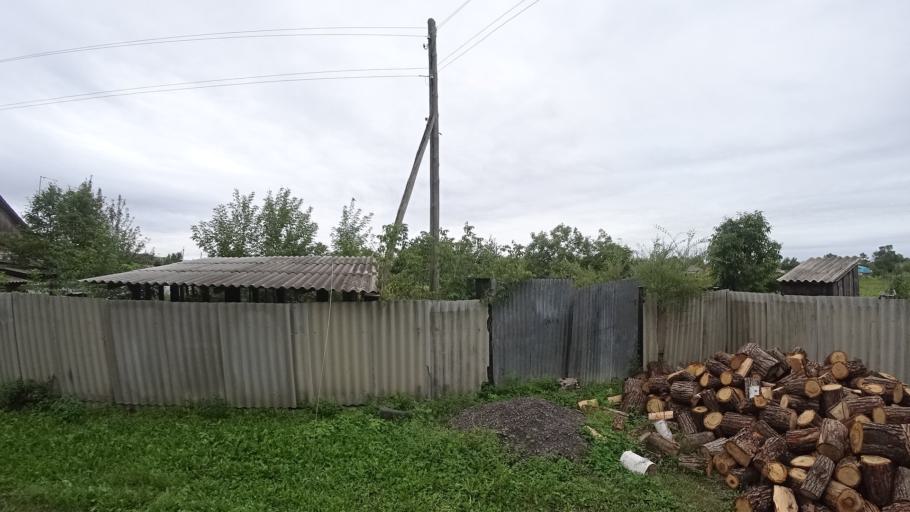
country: RU
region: Primorskiy
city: Chernigovka
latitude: 44.3480
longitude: 132.5792
